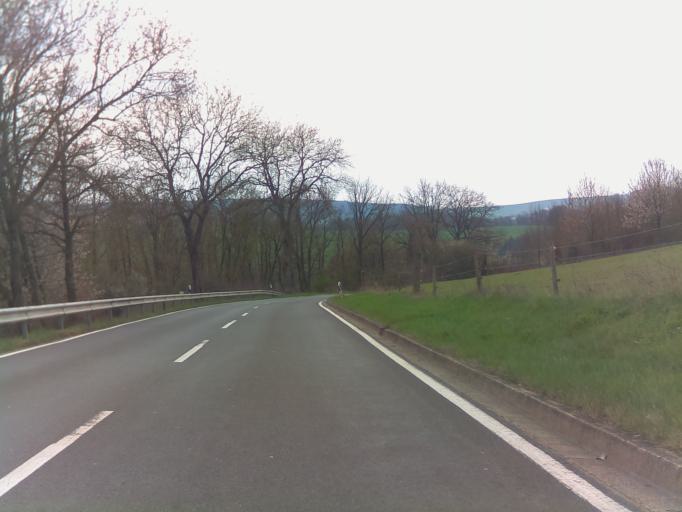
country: DE
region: Rheinland-Pfalz
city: Bruschied
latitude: 49.8344
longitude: 7.3887
